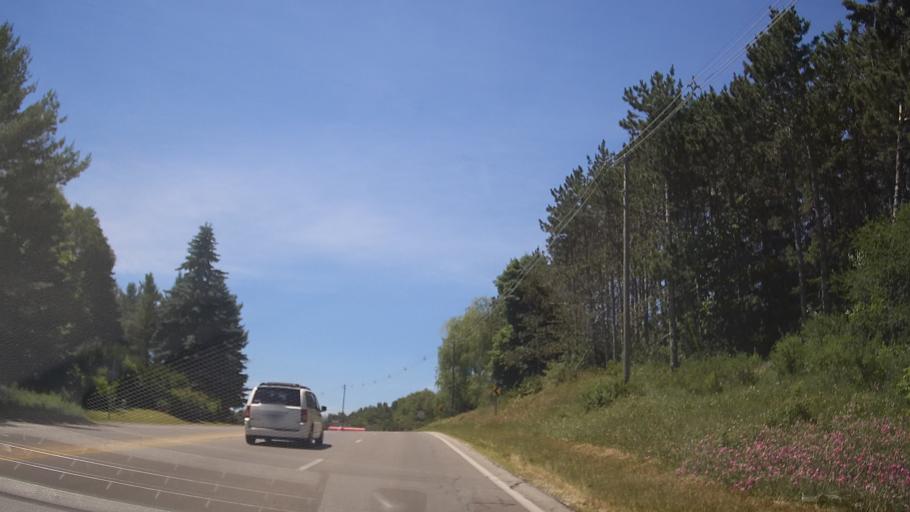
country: US
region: Michigan
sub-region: Grand Traverse County
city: Traverse City
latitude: 44.7262
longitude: -85.6737
